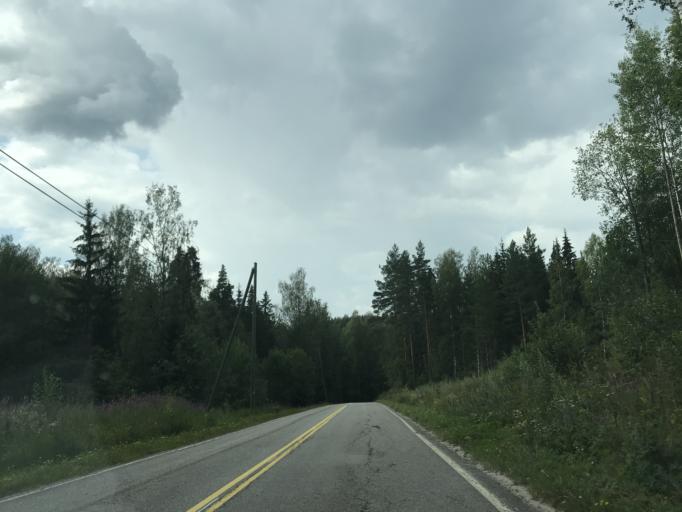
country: FI
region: Uusimaa
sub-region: Helsinki
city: Vihti
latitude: 60.3918
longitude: 24.3340
